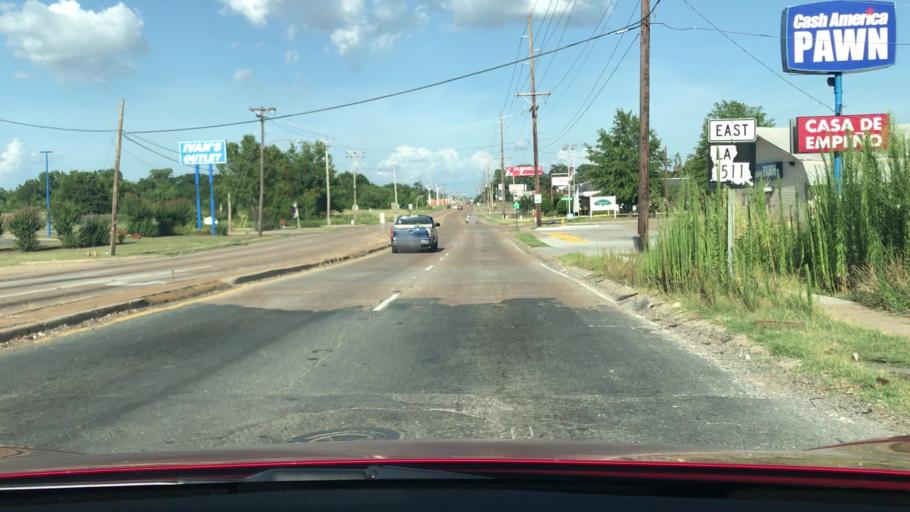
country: US
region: Louisiana
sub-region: Bossier Parish
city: Bossier City
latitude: 32.4419
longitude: -93.7807
